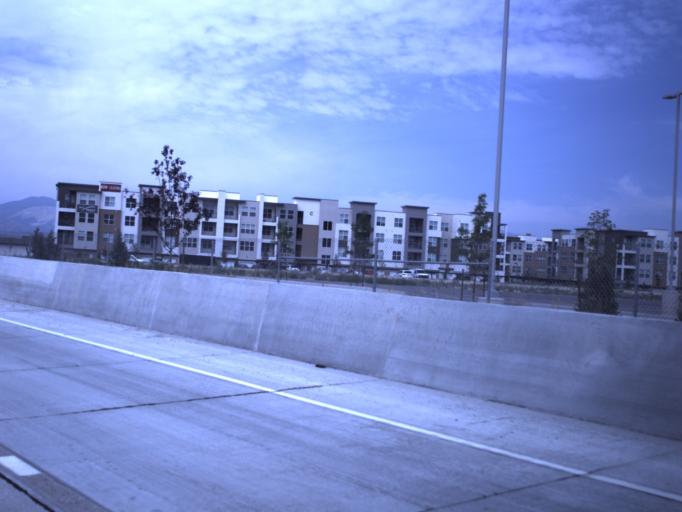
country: US
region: Utah
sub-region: Salt Lake County
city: Bluffdale
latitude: 40.5041
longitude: -111.9022
